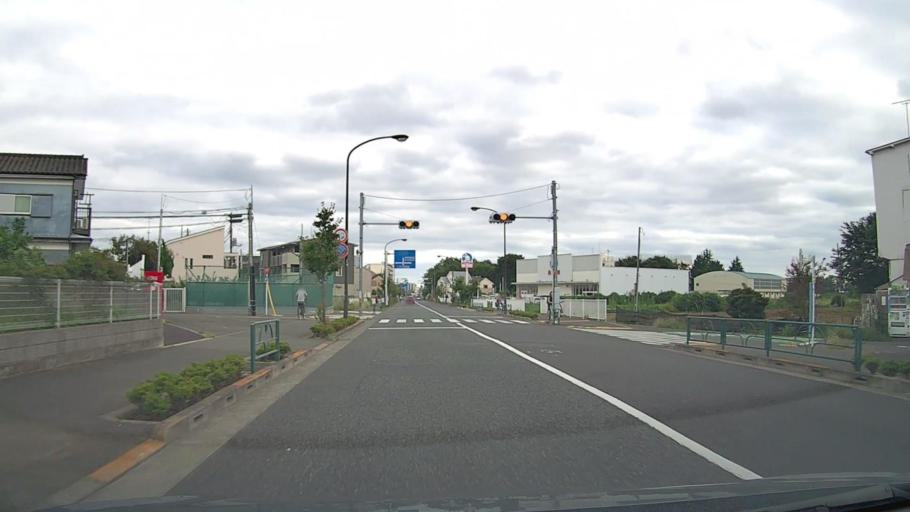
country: JP
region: Tokyo
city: Tanashicho
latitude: 35.7429
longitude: 139.5220
